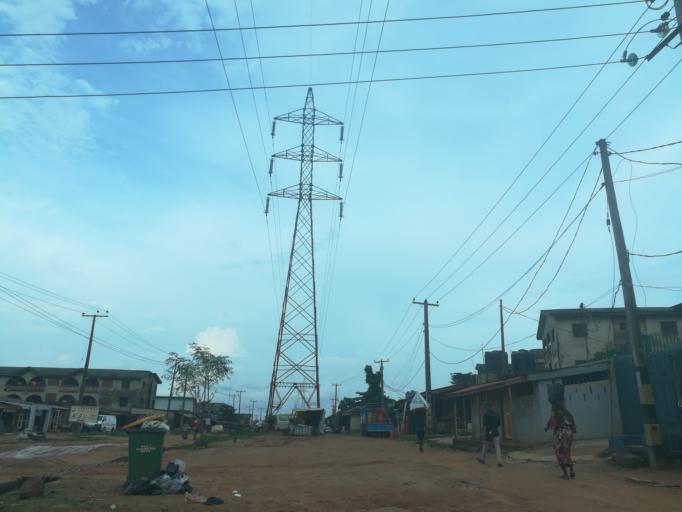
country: NG
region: Lagos
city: Ikorodu
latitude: 6.6259
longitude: 3.4980
